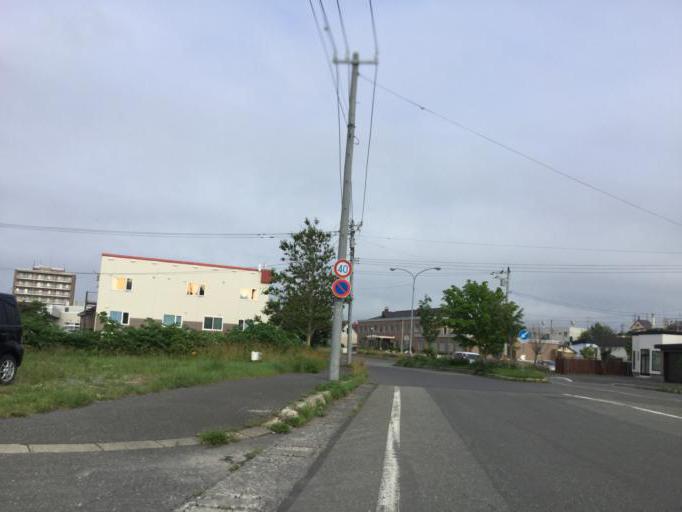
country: JP
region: Hokkaido
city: Wakkanai
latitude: 45.3941
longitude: 141.6952
